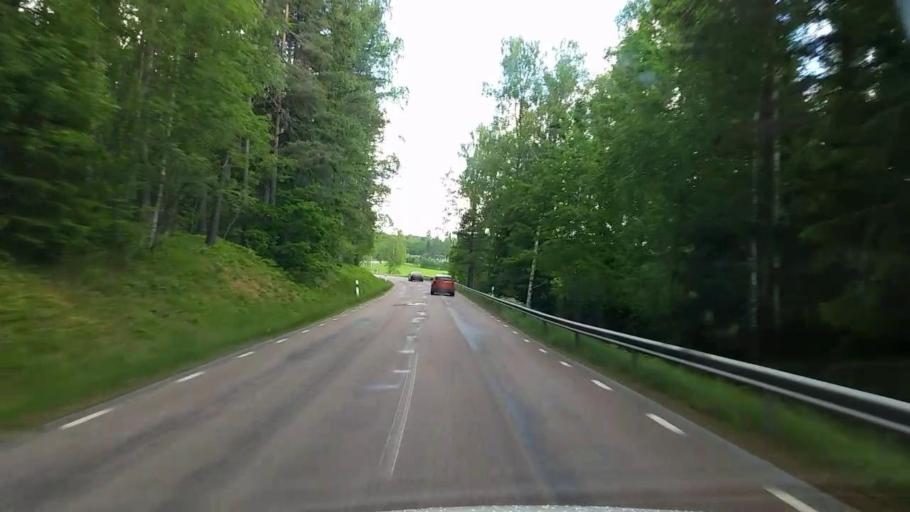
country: SE
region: Vaestmanland
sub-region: Skinnskattebergs Kommun
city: Skinnskatteberg
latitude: 59.8524
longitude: 15.8437
